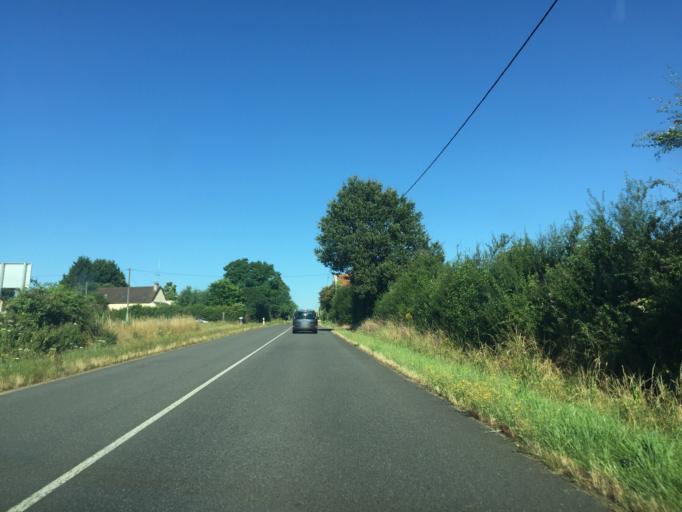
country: FR
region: Auvergne
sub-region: Departement de l'Allier
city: Dompierre-sur-Besbre
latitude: 46.5327
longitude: 3.6530
